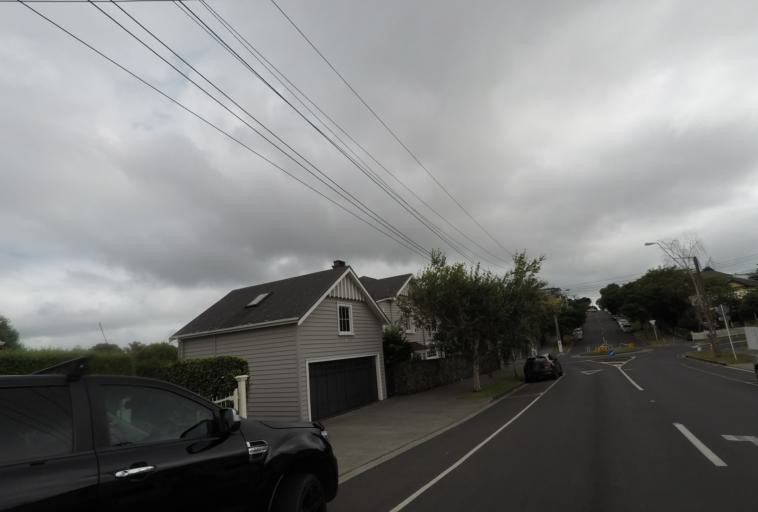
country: NZ
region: Auckland
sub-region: Auckland
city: Auckland
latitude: -36.8757
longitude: 174.7577
